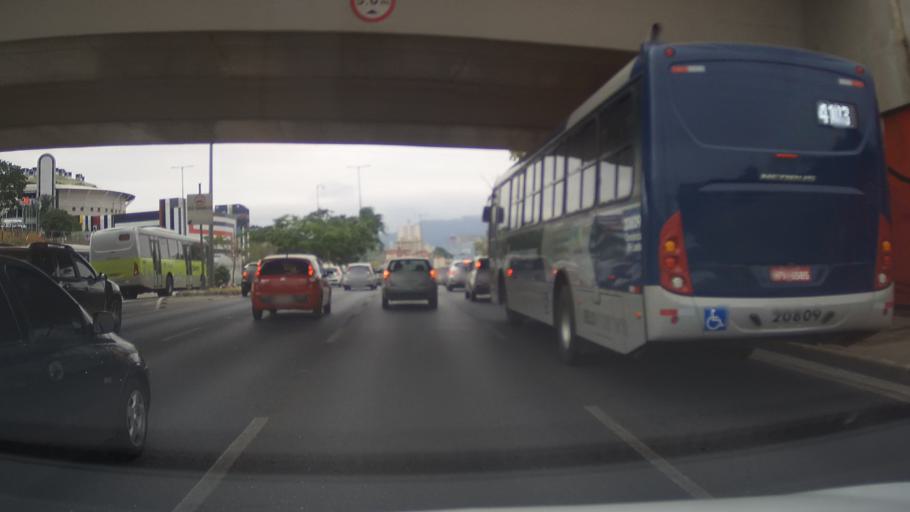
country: BR
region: Minas Gerais
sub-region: Belo Horizonte
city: Belo Horizonte
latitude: -19.8994
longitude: -43.9469
